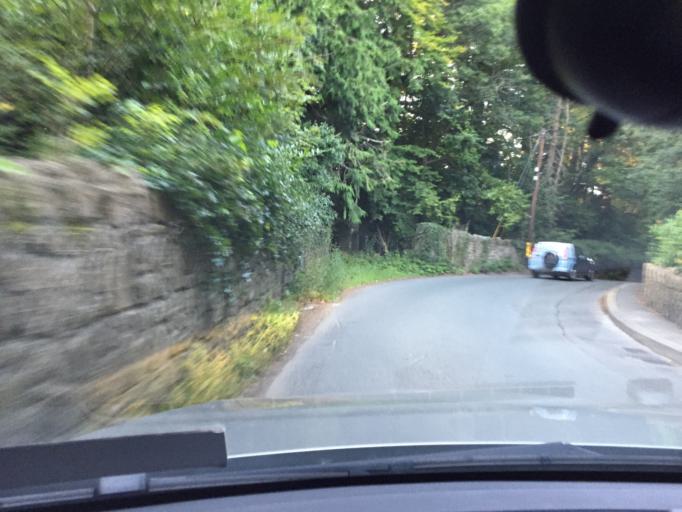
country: IE
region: Leinster
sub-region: Wicklow
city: Enniskerry
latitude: 53.1742
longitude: -6.1776
